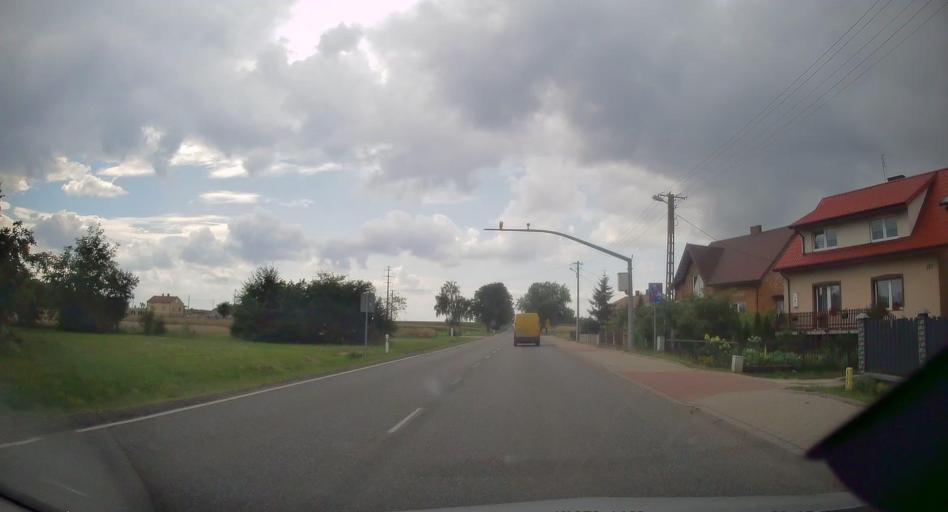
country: PL
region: Lodz Voivodeship
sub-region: Powiat skierniewicki
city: Gluchow
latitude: 51.7753
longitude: 20.1245
